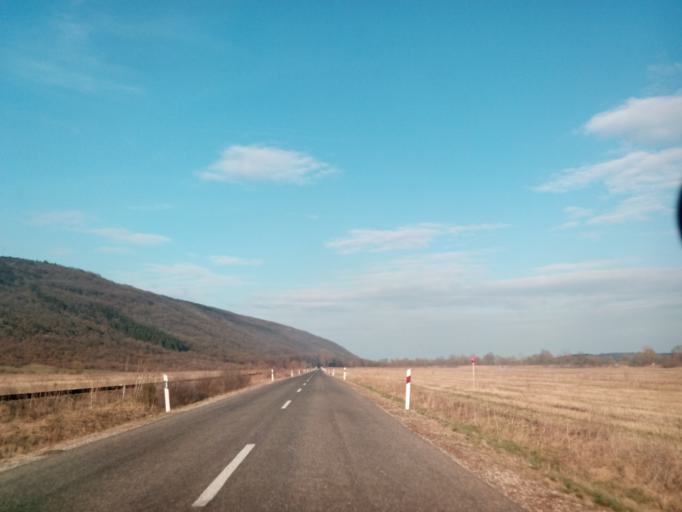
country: HU
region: Borsod-Abauj-Zemplen
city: Szendro
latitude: 48.5603
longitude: 20.7932
